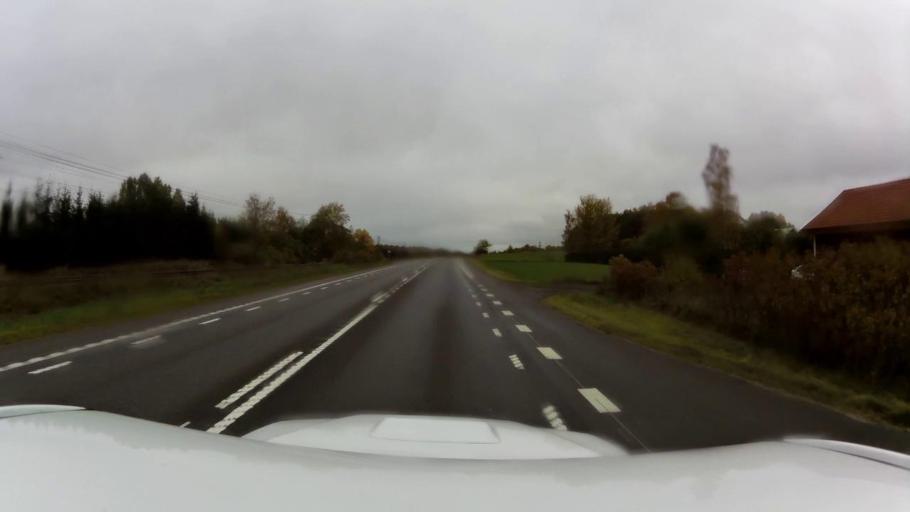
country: SE
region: OEstergoetland
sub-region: Linkopings Kommun
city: Linghem
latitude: 58.4549
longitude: 15.8489
